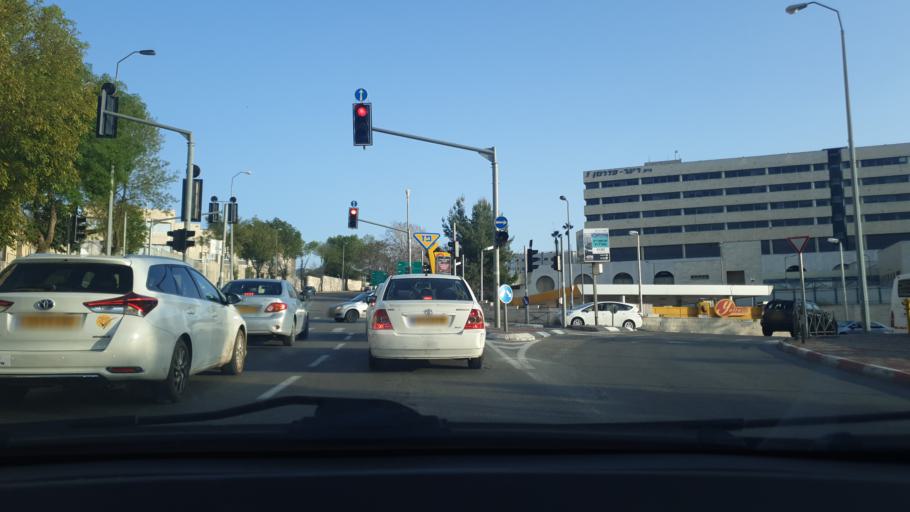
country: PS
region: West Bank
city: Bayt Iksa
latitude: 31.7895
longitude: 35.1891
